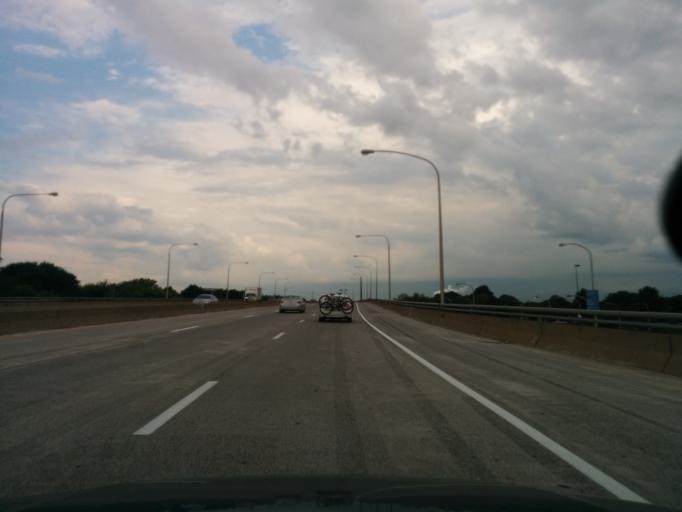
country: US
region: New Jersey
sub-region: Gloucester County
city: National Park
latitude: 39.8989
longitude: -75.1725
